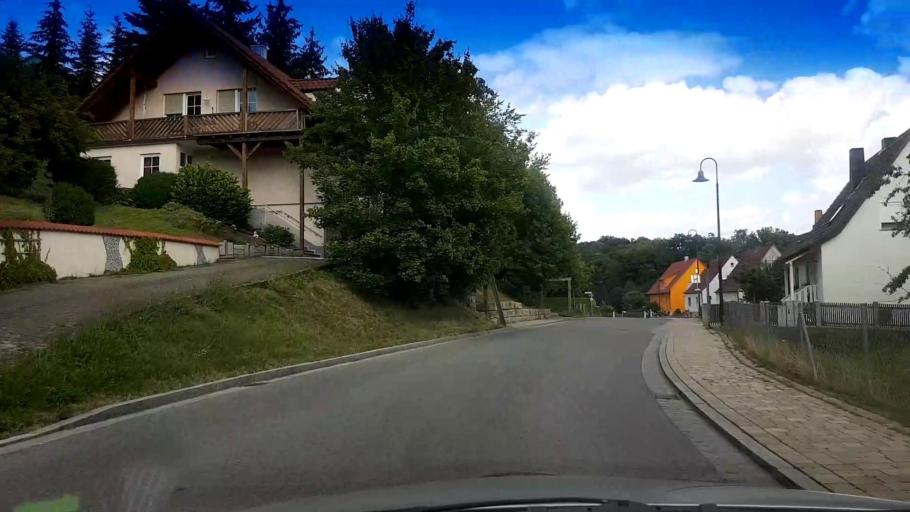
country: DE
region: Bavaria
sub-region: Upper Franconia
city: Reckendorf
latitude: 50.0003
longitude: 10.8104
